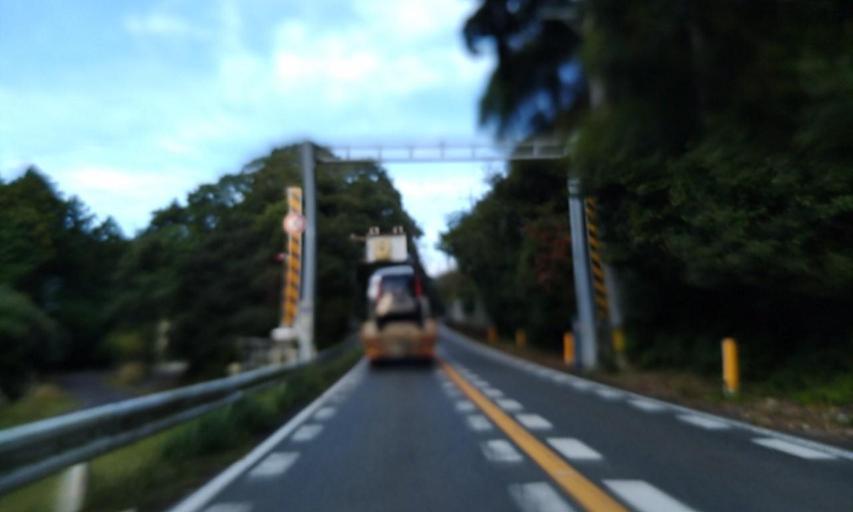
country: JP
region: Mie
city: Toba
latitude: 34.3964
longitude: 136.7859
